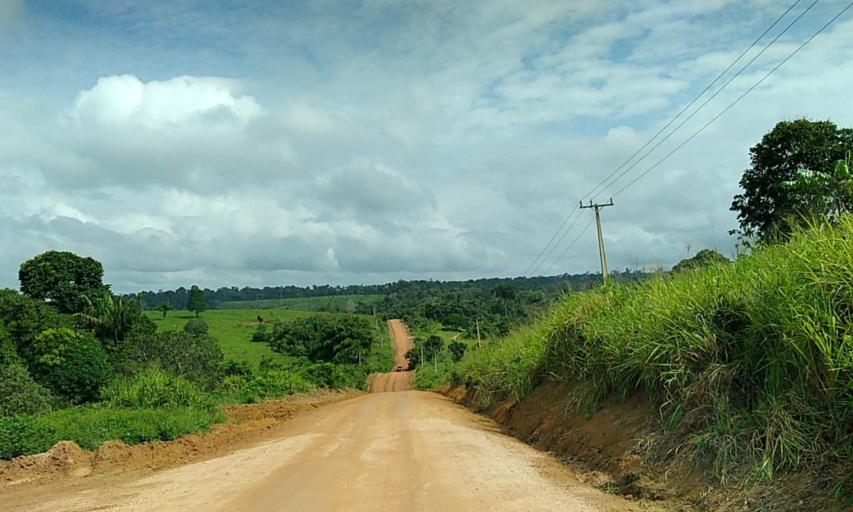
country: BR
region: Para
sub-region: Senador Jose Porfirio
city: Senador Jose Porfirio
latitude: -3.0635
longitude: -51.6351
